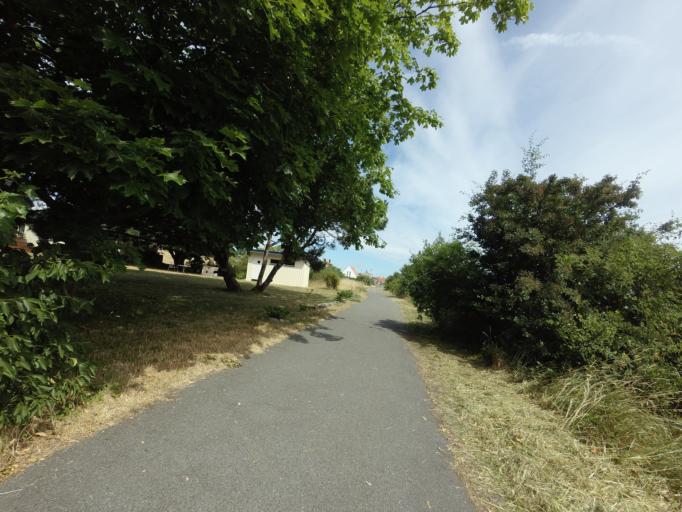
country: SE
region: Skane
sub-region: Simrishamns Kommun
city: Simrishamn
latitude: 55.5413
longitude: 14.3563
